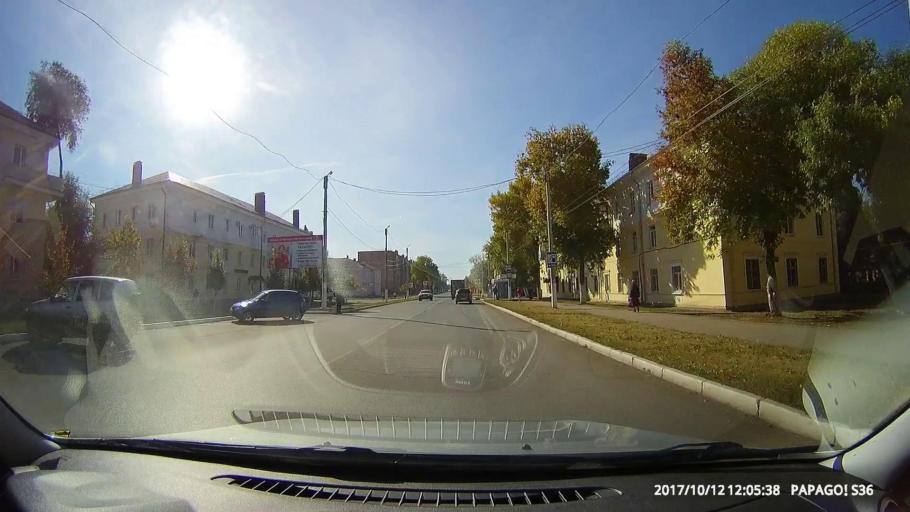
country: RU
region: Samara
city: Chapayevsk
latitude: 52.9760
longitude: 49.7108
